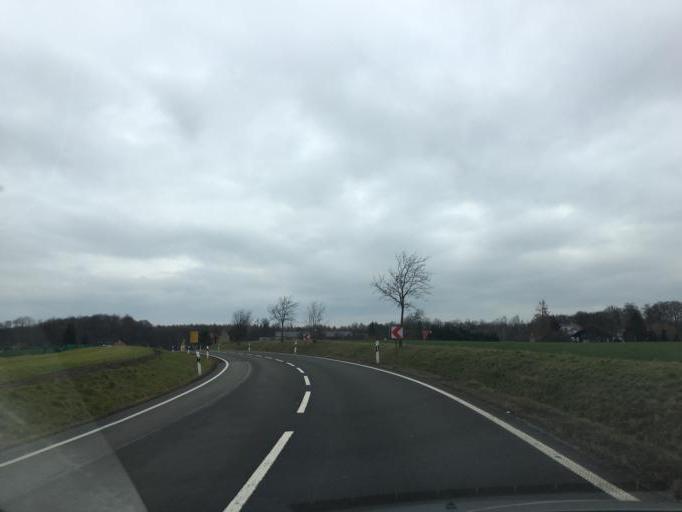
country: DE
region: Thuringia
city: Nobitz
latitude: 50.9552
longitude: 12.5142
